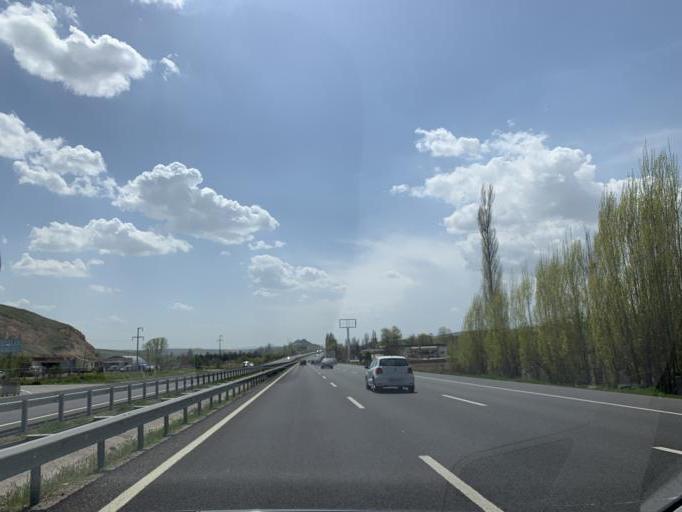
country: TR
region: Ankara
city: Temelli
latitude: 39.7937
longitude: 32.5299
